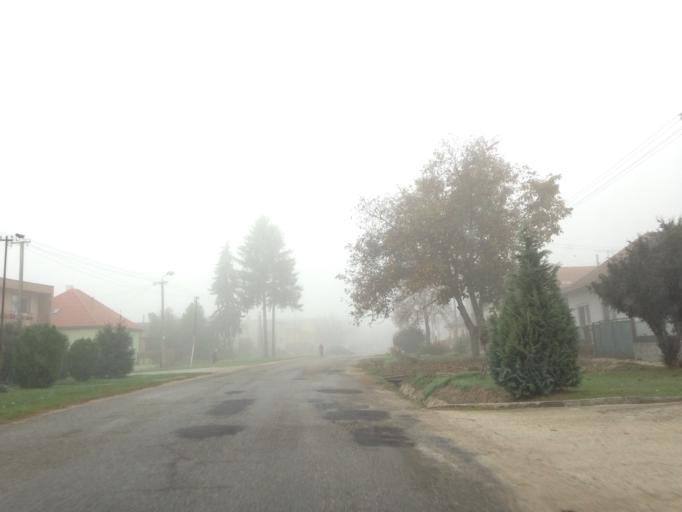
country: SK
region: Nitriansky
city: Svodin
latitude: 47.9035
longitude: 18.4162
